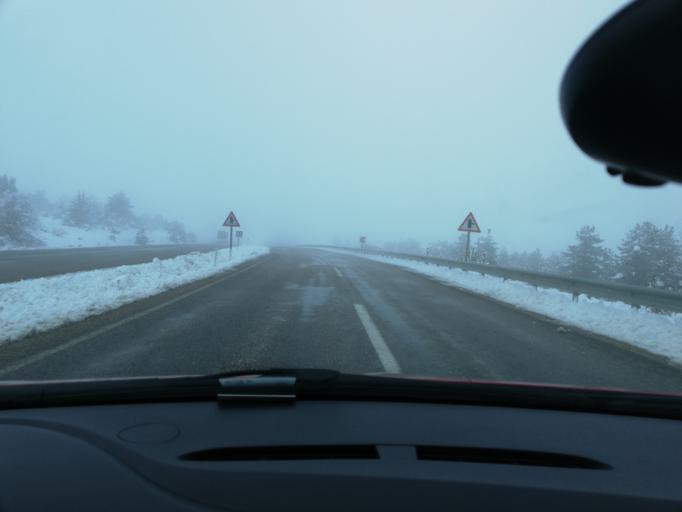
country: TR
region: Kastamonu
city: Akkaya
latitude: 41.2976
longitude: 33.5035
